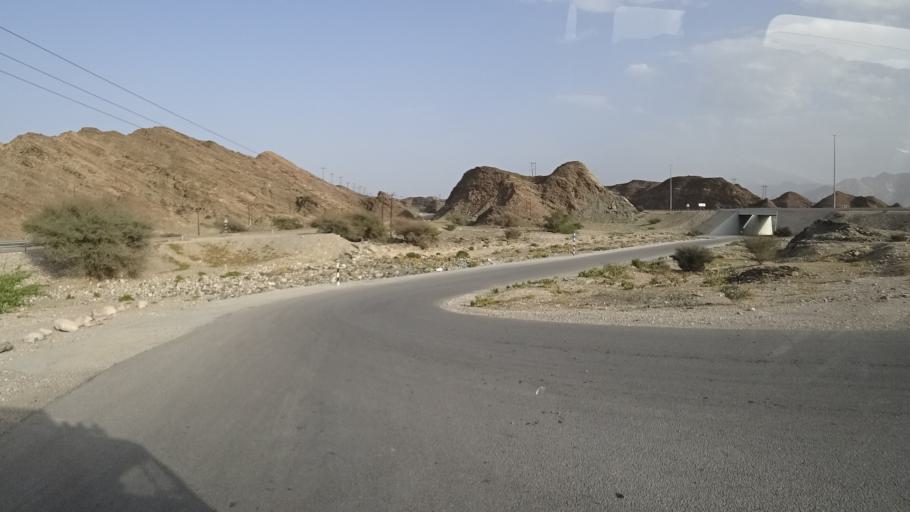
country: OM
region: Muhafazat Masqat
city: Bawshar
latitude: 23.3542
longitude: 58.5349
